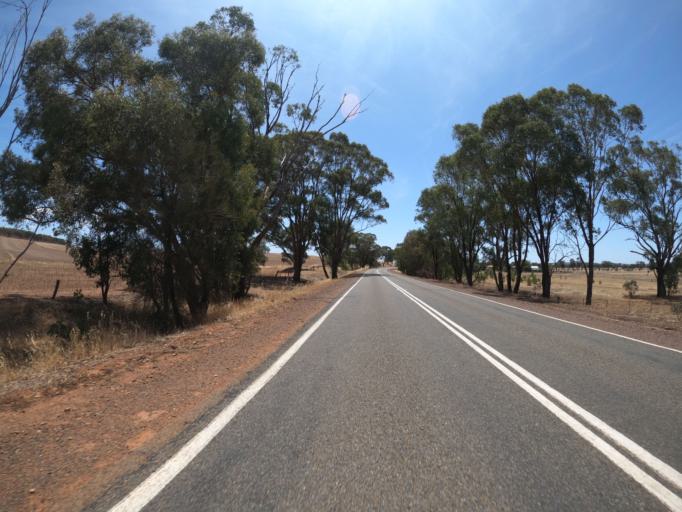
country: AU
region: Victoria
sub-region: Benalla
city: Benalla
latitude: -36.3247
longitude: 145.9594
